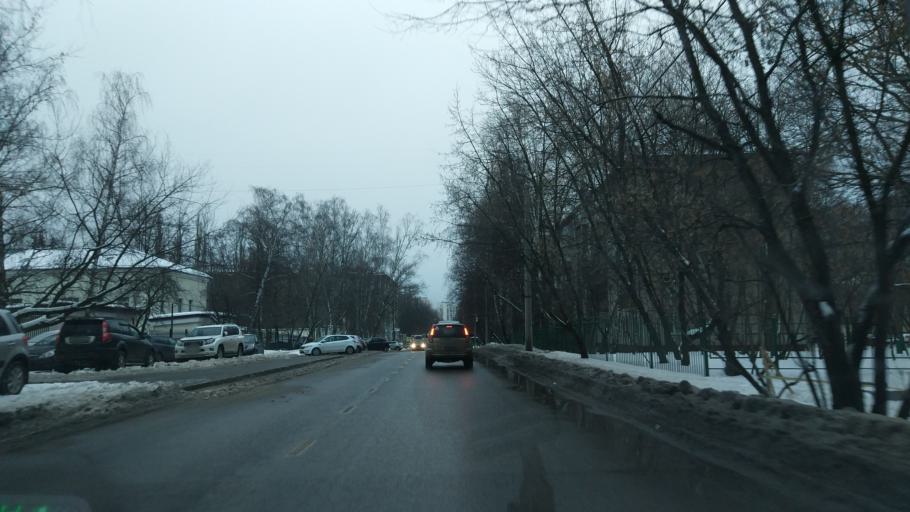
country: RU
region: Moskovskaya
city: Izmaylovo
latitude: 55.7898
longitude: 37.8235
